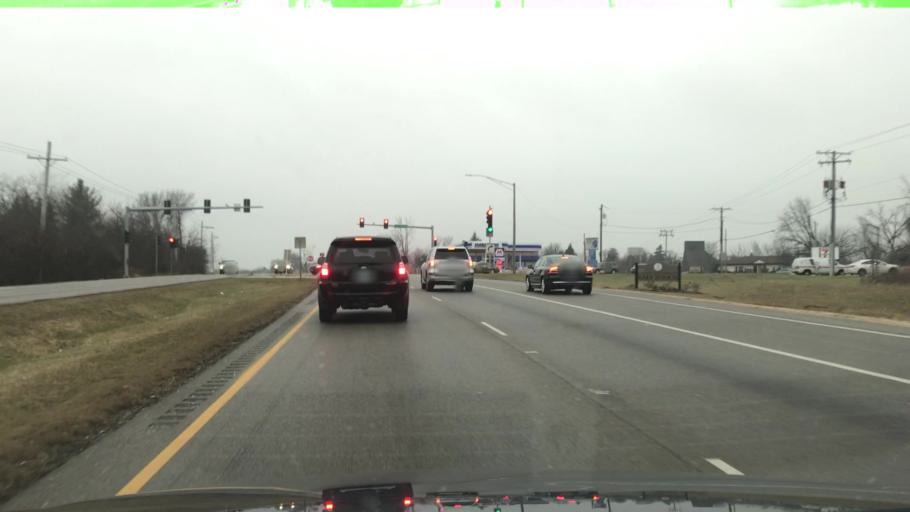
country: US
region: Illinois
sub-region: Lake County
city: Deer Park
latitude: 42.1785
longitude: -88.0770
